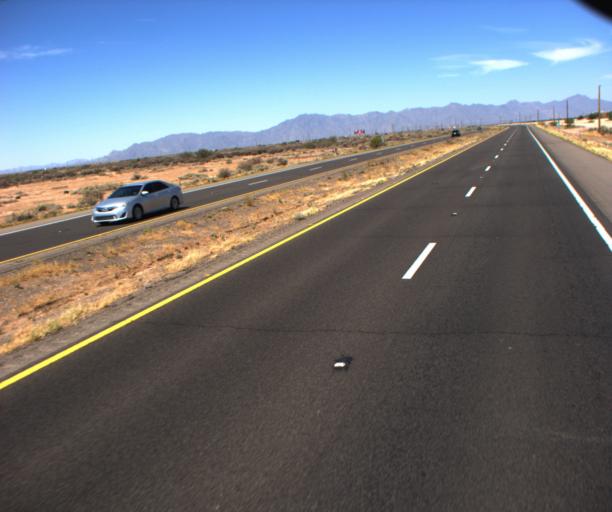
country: US
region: Arizona
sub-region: Maricopa County
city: Sun Lakes
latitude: 33.2522
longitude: -111.9680
